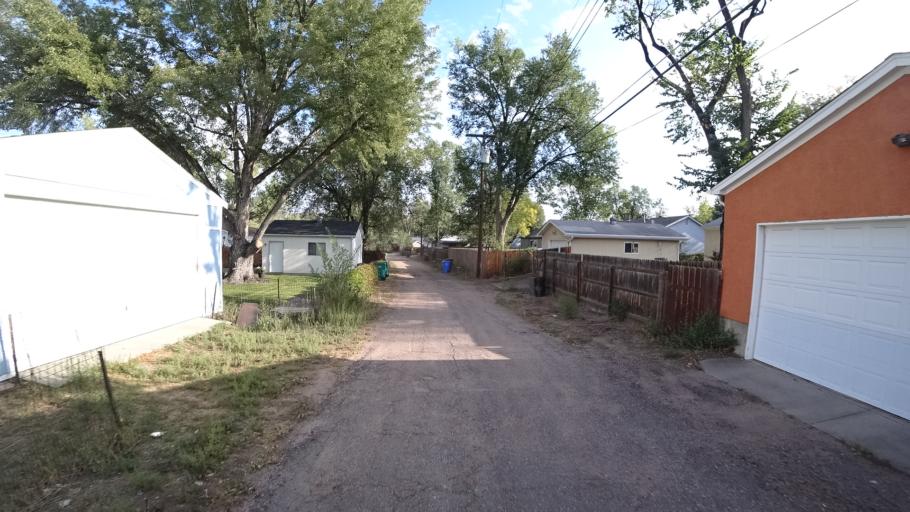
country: US
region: Colorado
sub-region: El Paso County
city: Colorado Springs
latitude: 38.8574
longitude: -104.7703
